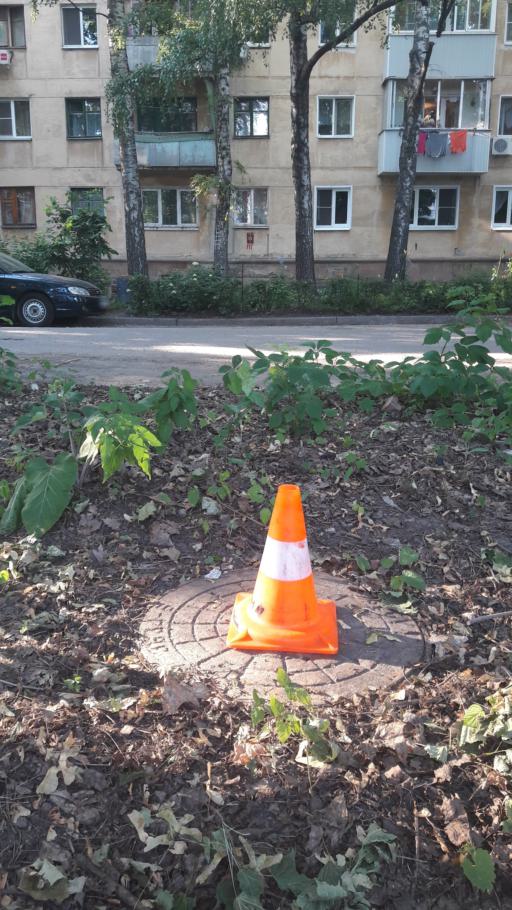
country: RU
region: Voronezj
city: Voronezh
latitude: 51.6751
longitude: 39.1961
